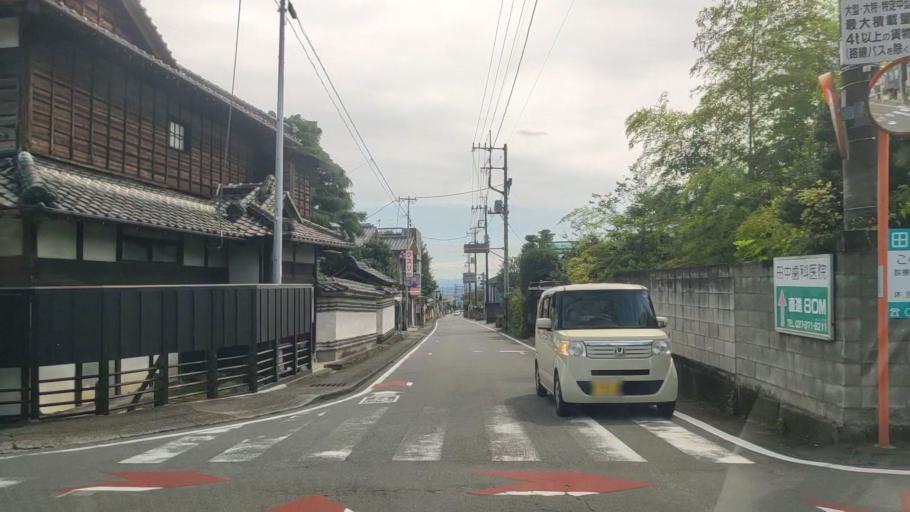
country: JP
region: Gunma
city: Kanekomachi
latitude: 36.3941
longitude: 138.9566
